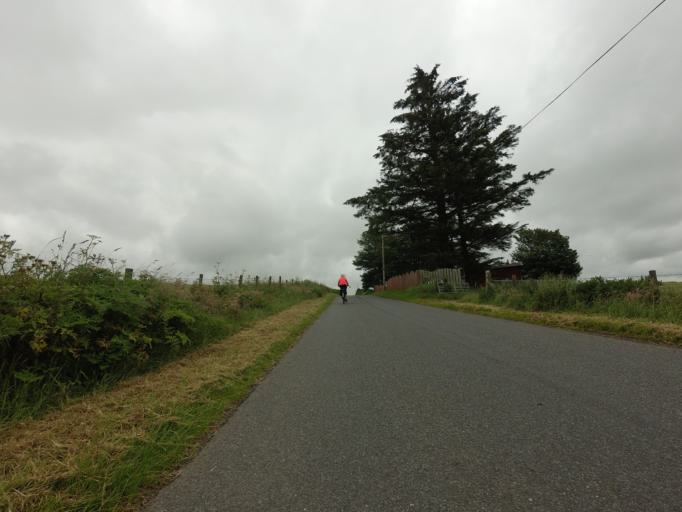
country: GB
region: Scotland
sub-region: Aberdeenshire
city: Turriff
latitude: 57.5438
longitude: -2.2570
